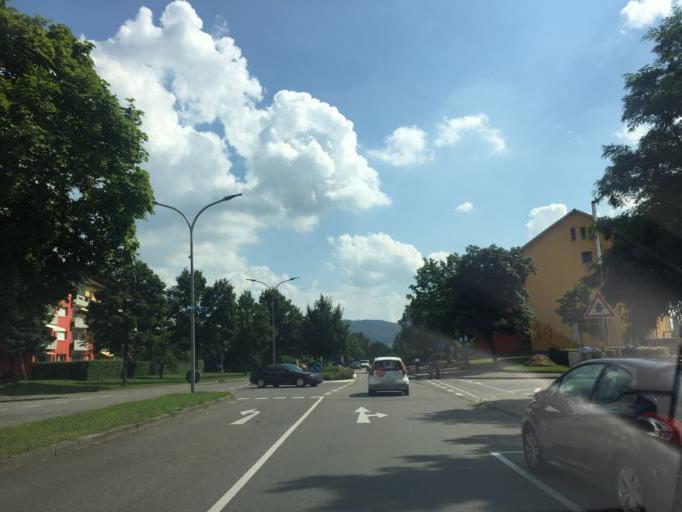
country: DE
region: Baden-Wuerttemberg
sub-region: Freiburg Region
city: Rielasingen-Worblingen
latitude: 47.7425
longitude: 8.8508
